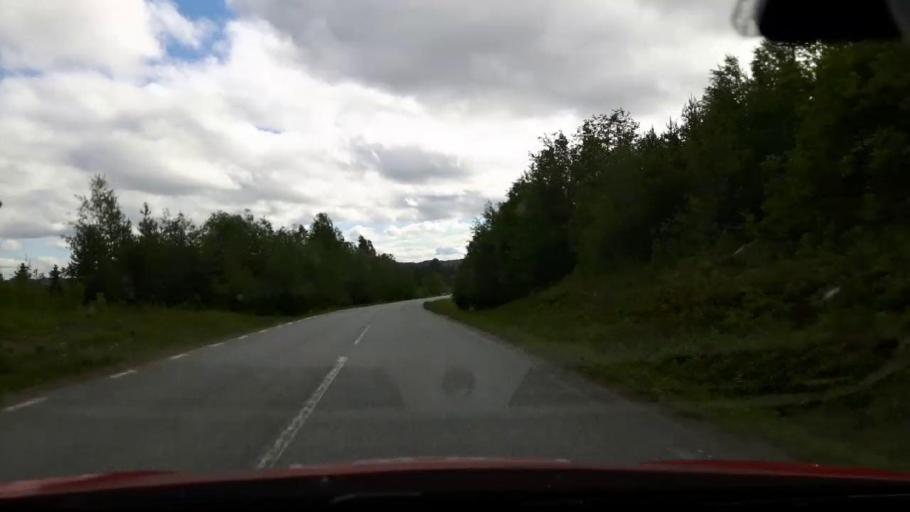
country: SE
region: Jaemtland
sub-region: Ragunda Kommun
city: Hammarstrand
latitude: 62.9719
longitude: 16.0663
